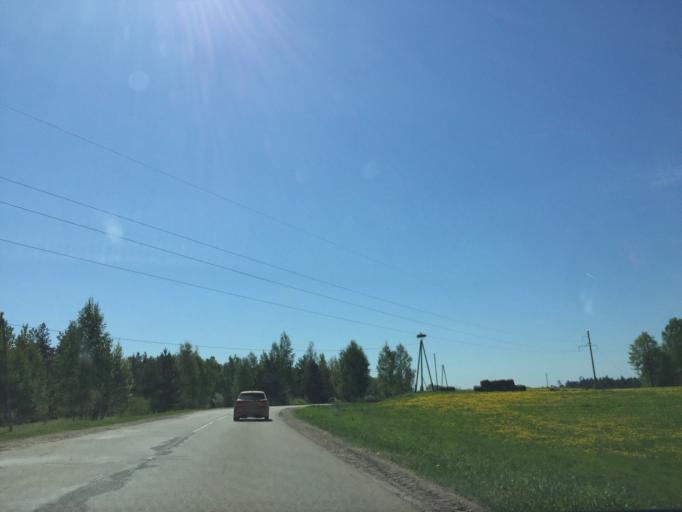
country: LV
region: Malpils
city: Malpils
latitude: 56.9269
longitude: 24.9370
